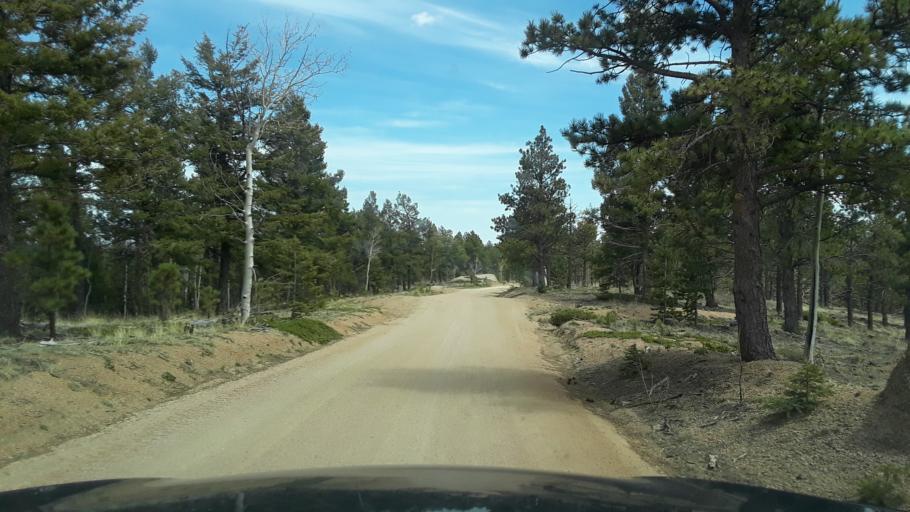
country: US
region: Colorado
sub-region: El Paso County
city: Palmer Lake
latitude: 39.0590
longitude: -104.9784
